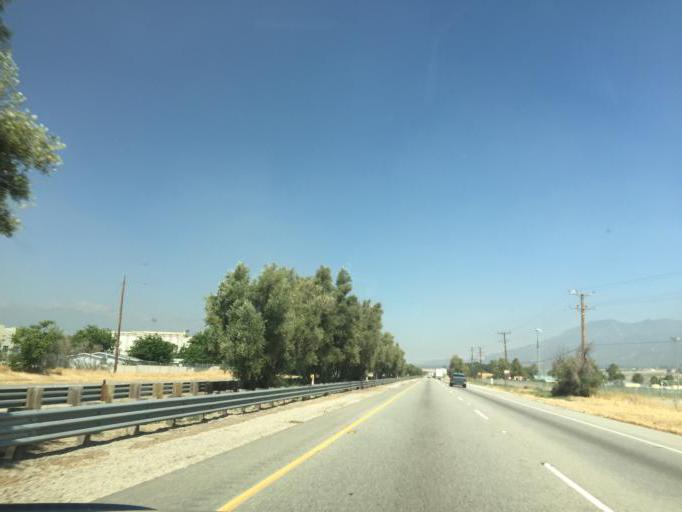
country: US
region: California
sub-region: San Bernardino County
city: Muscoy
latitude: 34.1959
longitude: -117.3678
